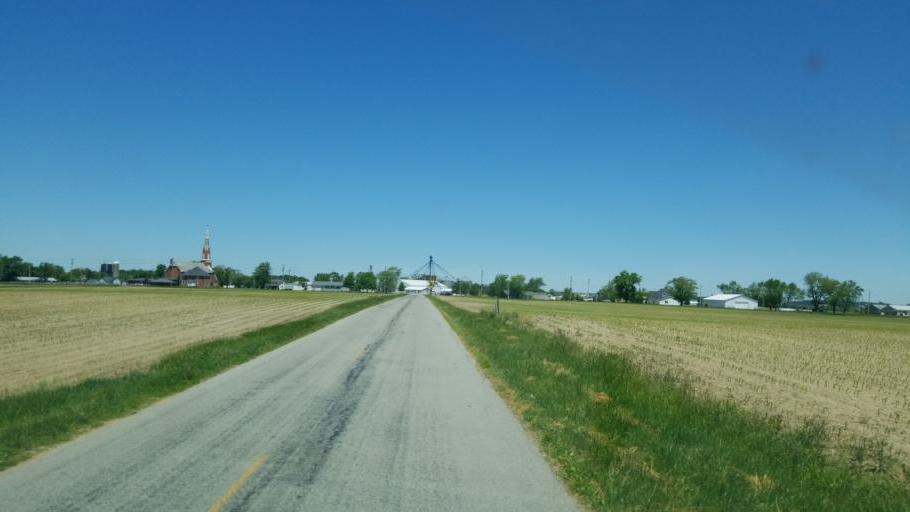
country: US
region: Ohio
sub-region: Mercer County
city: Fort Recovery
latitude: 40.3631
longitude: -84.7099
